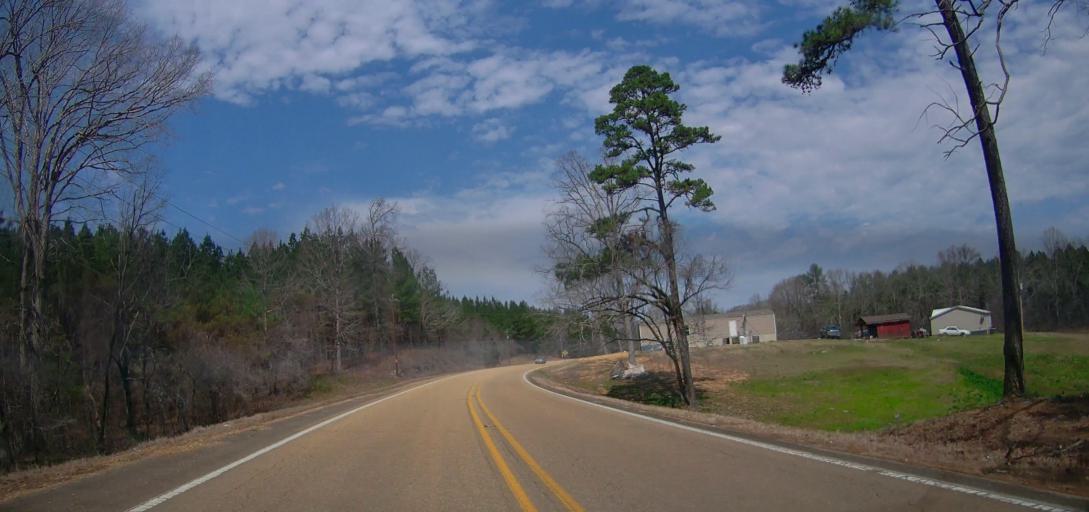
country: US
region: Mississippi
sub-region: Union County
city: New Albany
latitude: 34.6056
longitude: -89.1468
